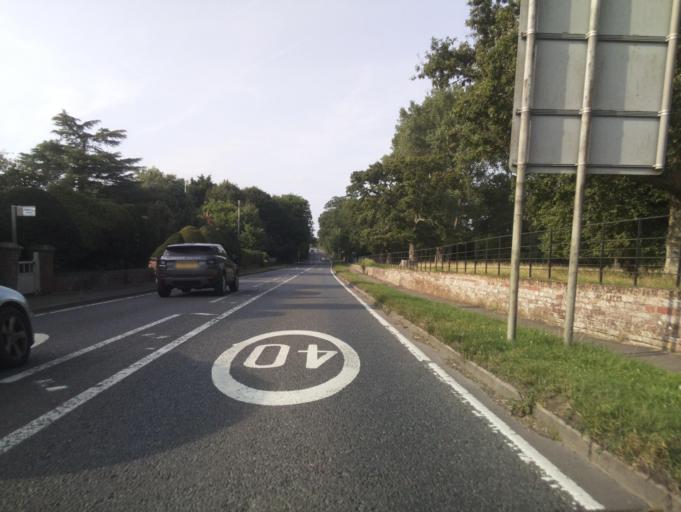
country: GB
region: England
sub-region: Warwickshire
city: Studley
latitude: 52.2433
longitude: -1.8845
